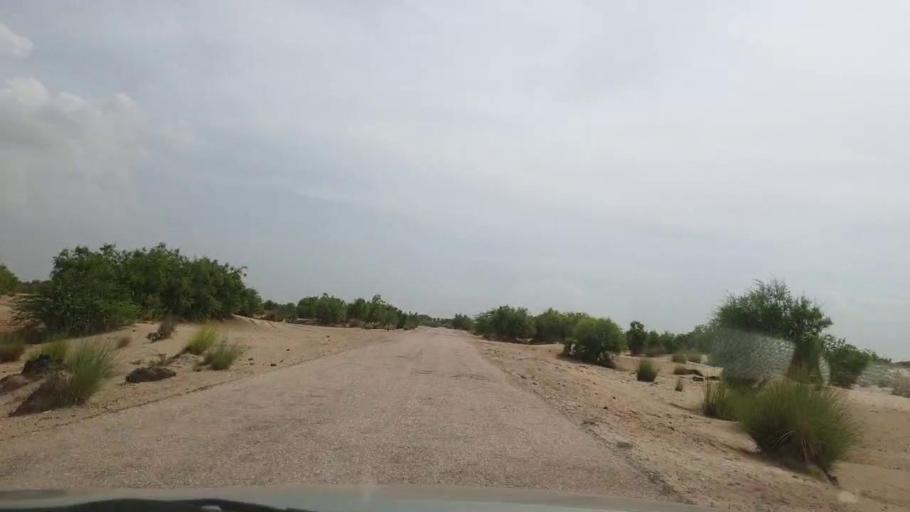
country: PK
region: Sindh
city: Bozdar
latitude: 27.0950
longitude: 69.0163
